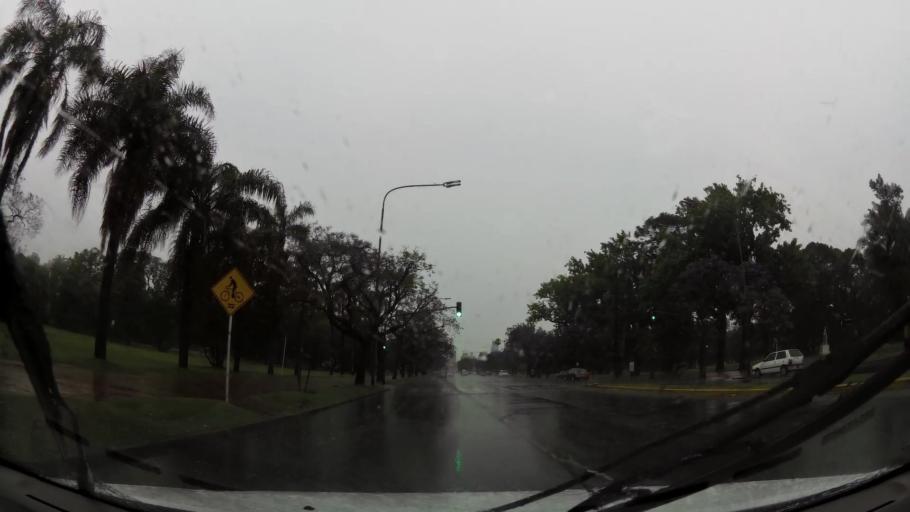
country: AR
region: Buenos Aires F.D.
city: Retiro
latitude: -34.5723
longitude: -58.4124
